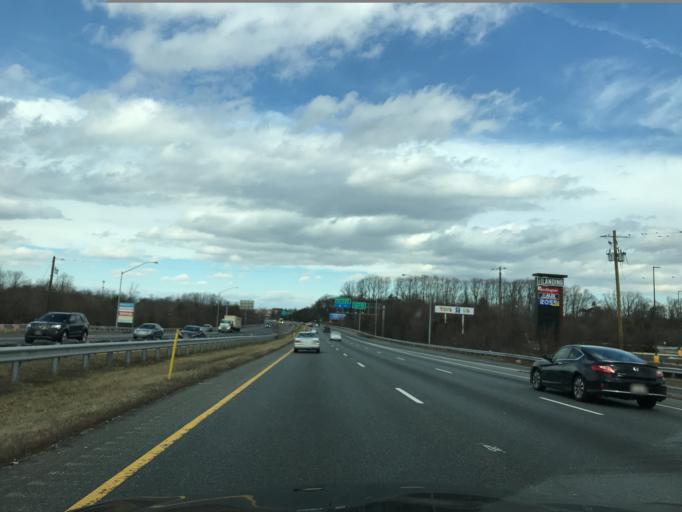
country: US
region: Maryland
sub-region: Prince George's County
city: Clinton
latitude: 38.7711
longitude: -76.8859
